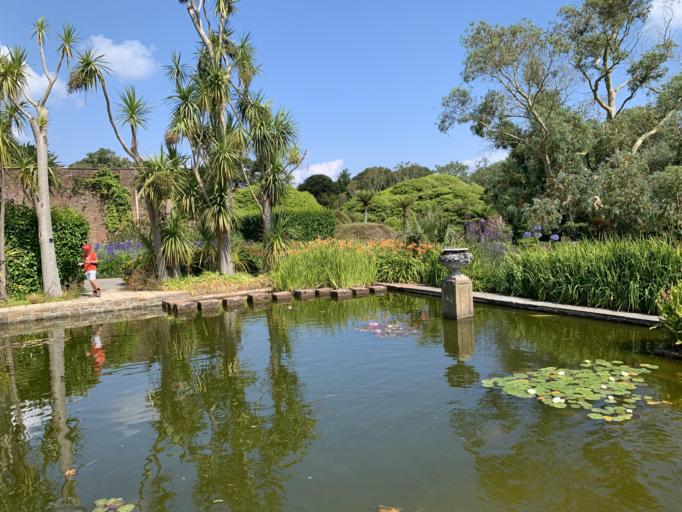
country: GB
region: Scotland
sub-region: Dumfries and Galloway
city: Stranraer
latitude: 54.7422
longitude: -4.9591
